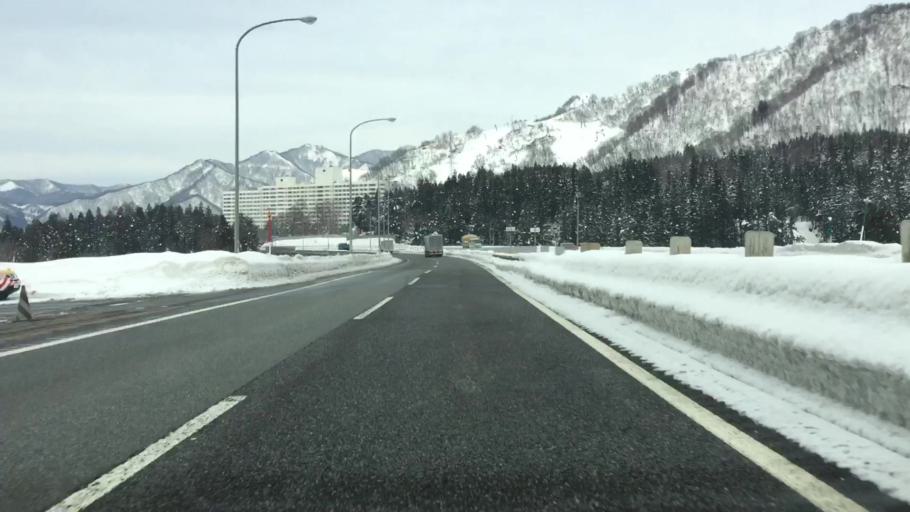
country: JP
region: Niigata
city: Shiozawa
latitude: 36.8990
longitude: 138.8463
